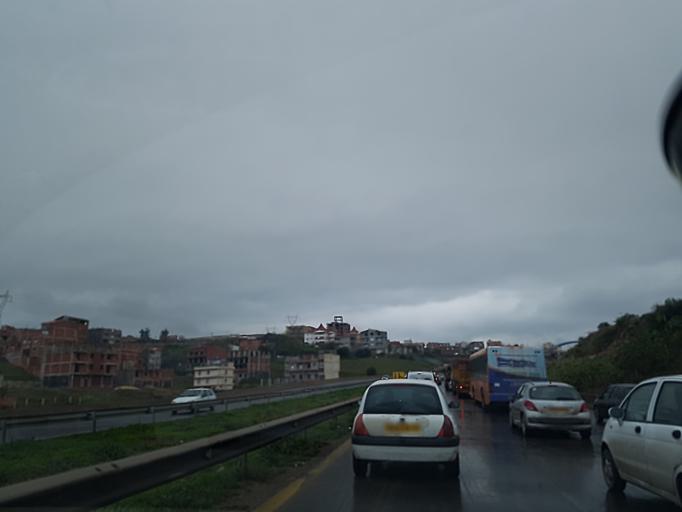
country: DZ
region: Boumerdes
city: Ouled Moussa
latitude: 36.6790
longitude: 3.3805
